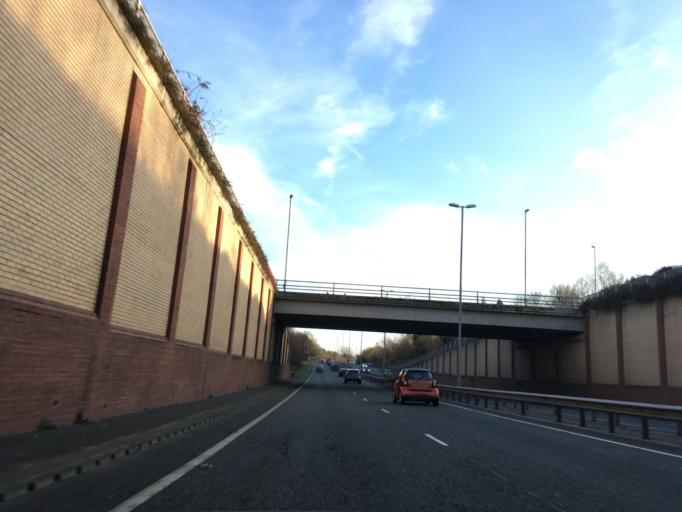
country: GB
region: England
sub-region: Borough of Stockport
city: Cheadle Hulme
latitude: 53.3802
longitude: -2.2186
